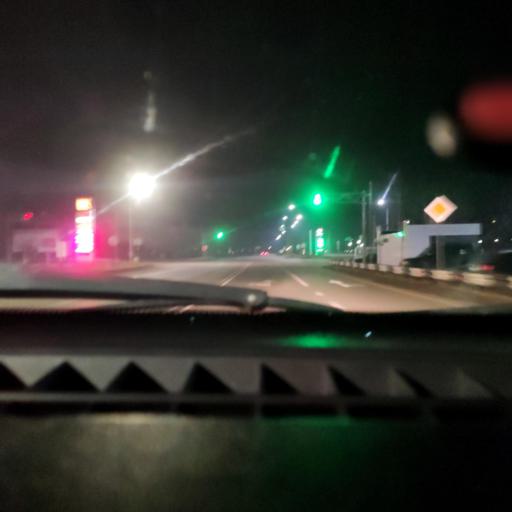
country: RU
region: Bashkortostan
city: Kushnarenkovo
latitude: 55.1007
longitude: 55.3335
